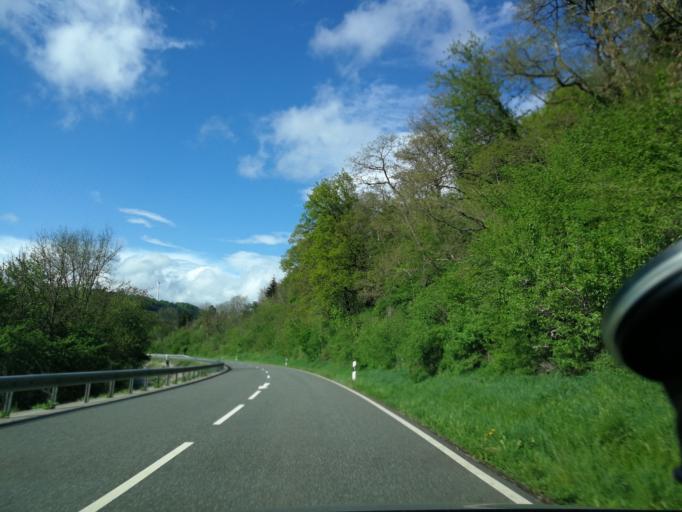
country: DE
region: Rheinland-Pfalz
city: Oberbillig
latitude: 49.7443
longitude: 6.5045
